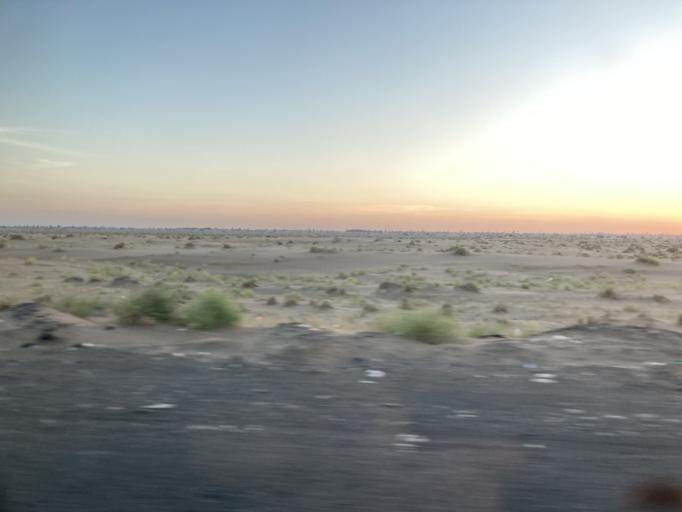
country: YE
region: Lahij
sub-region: Al  Hawtah
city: Lahij
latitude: 13.1036
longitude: 44.9020
